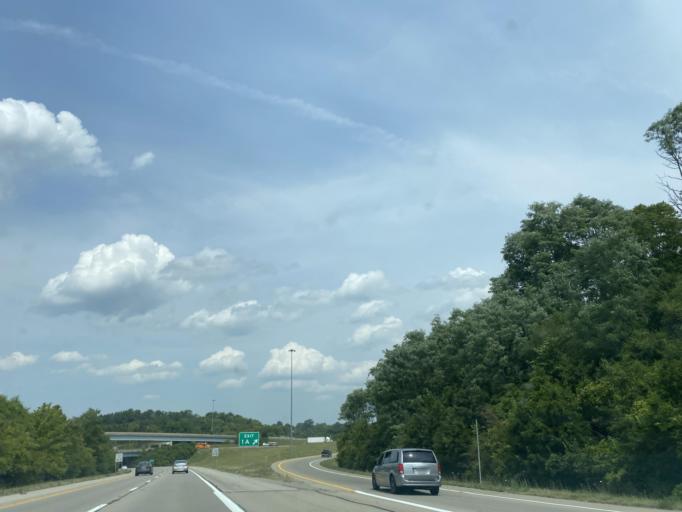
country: US
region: Kentucky
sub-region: Campbell County
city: Highland Heights
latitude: 39.0441
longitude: -84.4558
